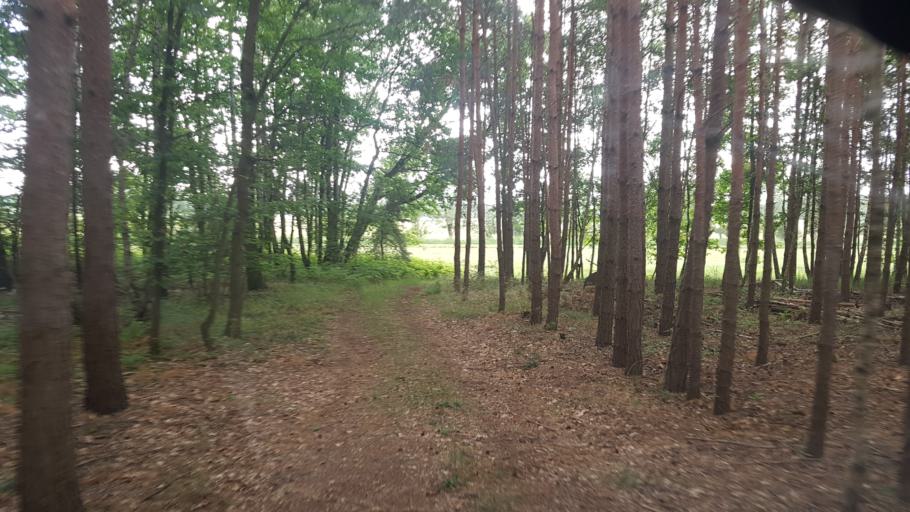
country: DE
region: Brandenburg
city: Finsterwalde
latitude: 51.6064
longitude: 13.6627
